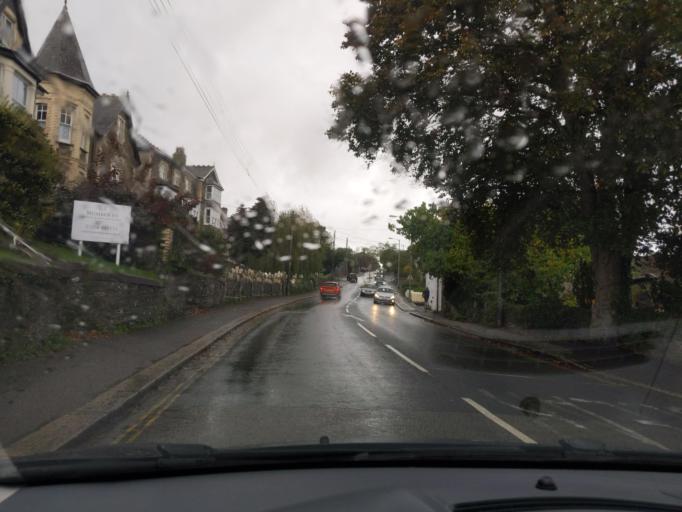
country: GB
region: England
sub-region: Cornwall
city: Wadebridge
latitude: 50.5164
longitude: -4.8399
